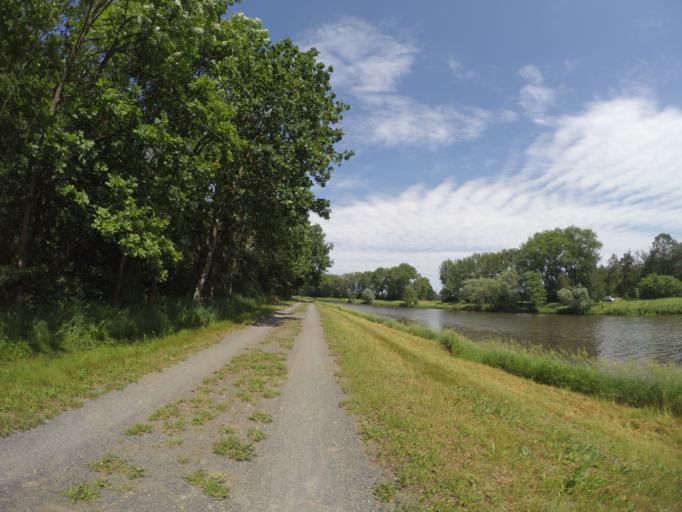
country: CZ
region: Central Bohemia
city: Poricany
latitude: 50.1661
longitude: 14.9192
